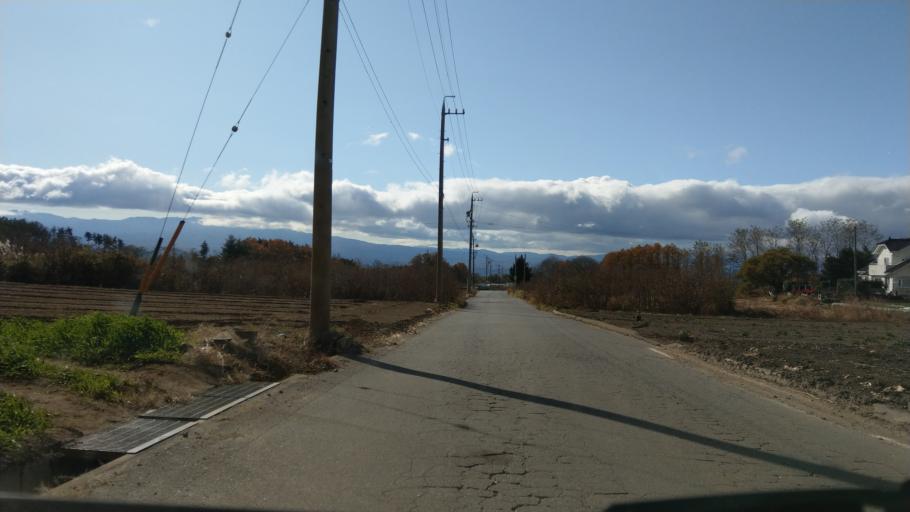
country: JP
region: Nagano
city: Komoro
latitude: 36.3160
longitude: 138.4812
